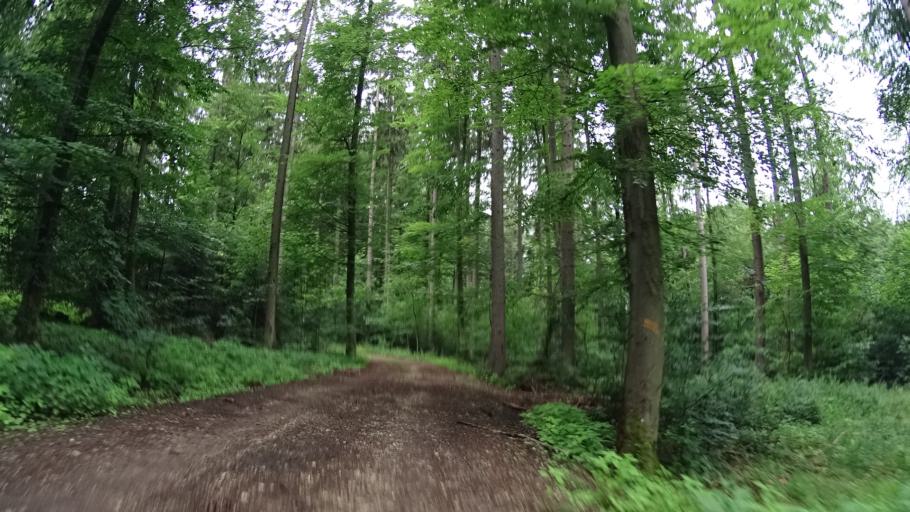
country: DE
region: Bavaria
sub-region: Upper Bavaria
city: Stammham
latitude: 48.8792
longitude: 11.4319
